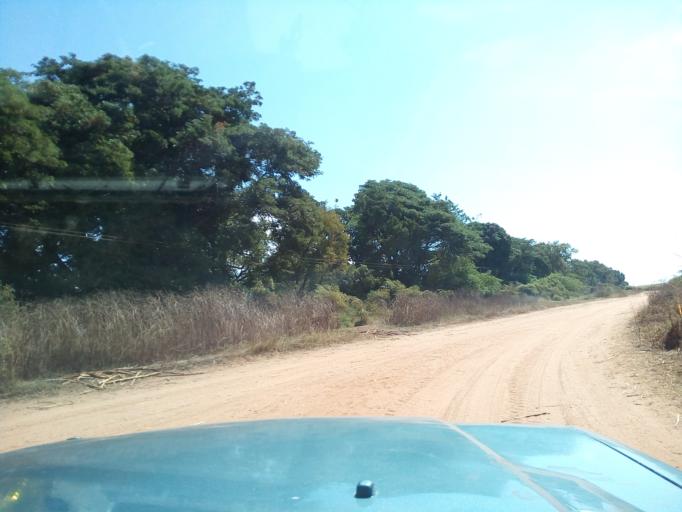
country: MG
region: Boeny
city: Mahajanga
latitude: -15.9528
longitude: 45.8982
